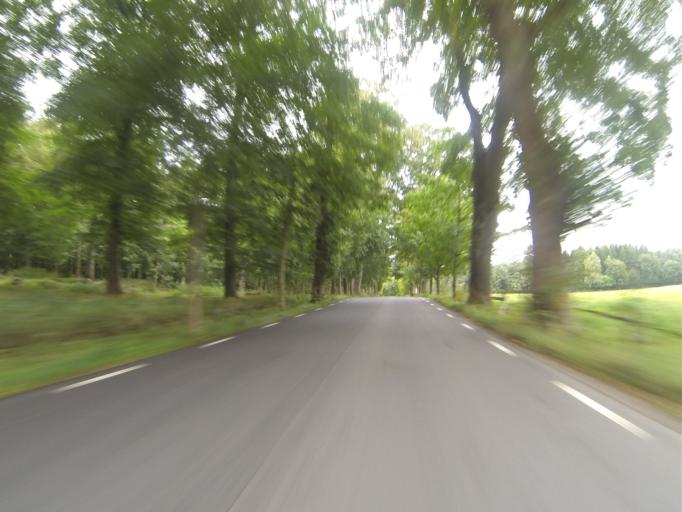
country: SE
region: Skane
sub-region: Lunds Kommun
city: Genarp
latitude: 55.6291
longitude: 13.4078
